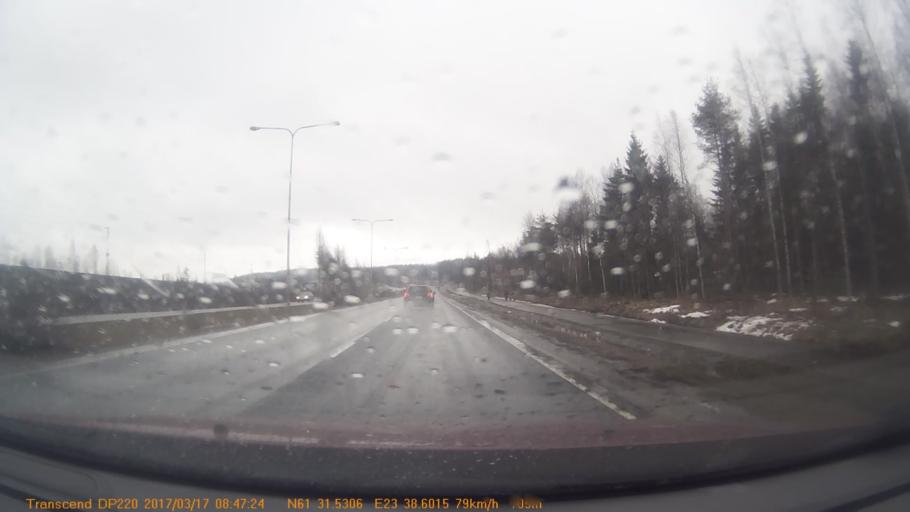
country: FI
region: Pirkanmaa
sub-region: Tampere
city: Yloejaervi
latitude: 61.5253
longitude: 23.6435
